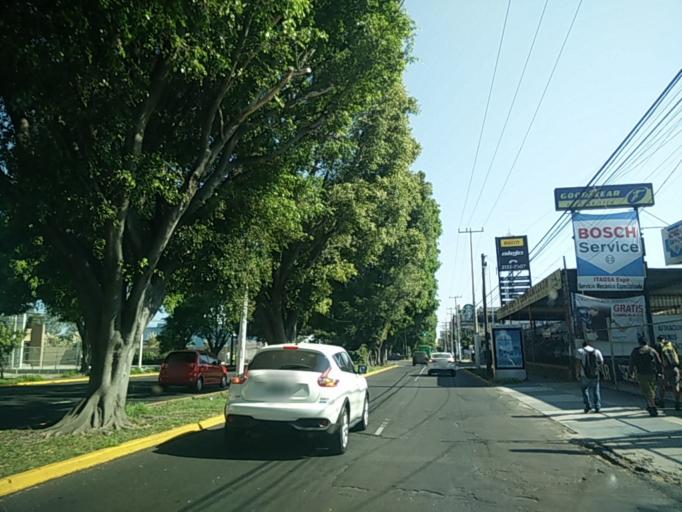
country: MX
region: Jalisco
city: Guadalajara
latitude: 20.6522
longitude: -103.3963
